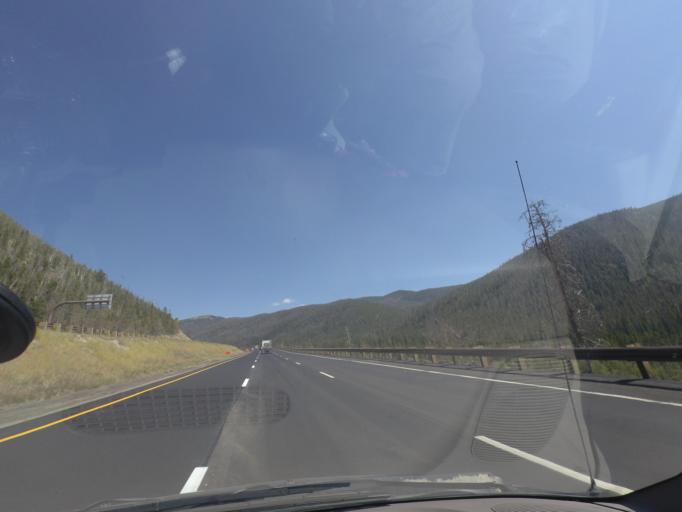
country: US
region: Colorado
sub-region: Summit County
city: Keystone
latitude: 39.6521
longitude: -106.0065
